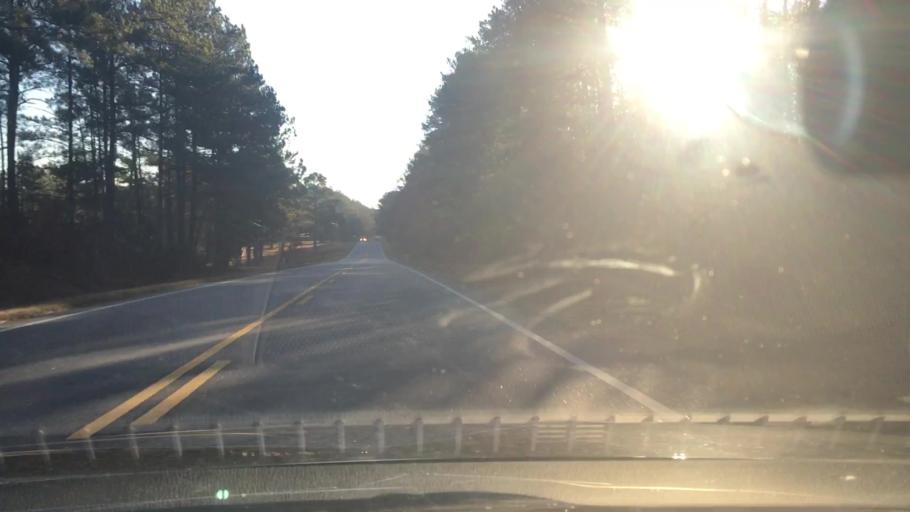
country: US
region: Georgia
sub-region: Coweta County
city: Senoia
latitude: 33.2601
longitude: -84.5085
